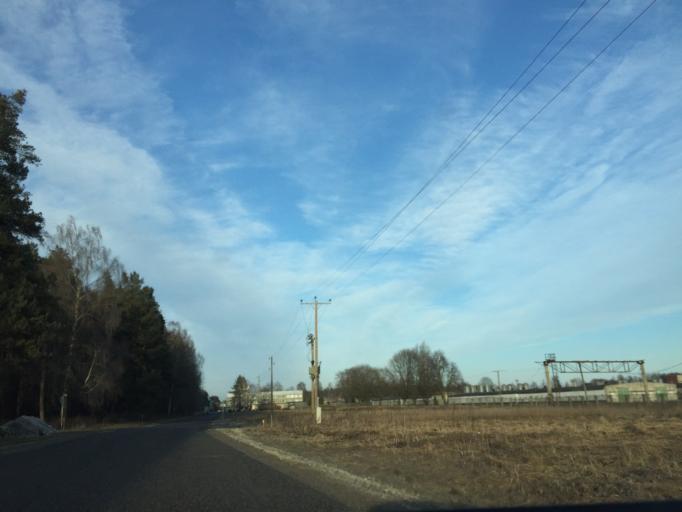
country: LV
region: Kekava
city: Kekava
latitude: 56.8261
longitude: 24.1926
